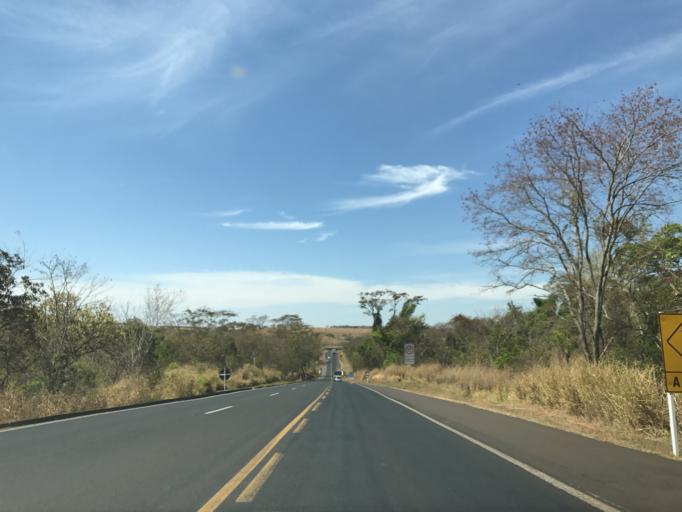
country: BR
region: Minas Gerais
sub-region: Monte Alegre De Minas
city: Monte Alegre de Minas
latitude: -18.9371
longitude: -49.0289
